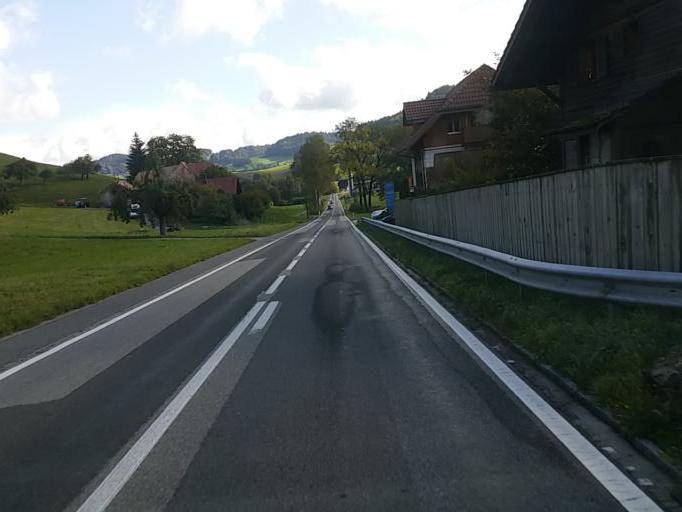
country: CH
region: Bern
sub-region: Oberaargau
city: Madiswil
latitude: 47.1542
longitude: 7.7781
